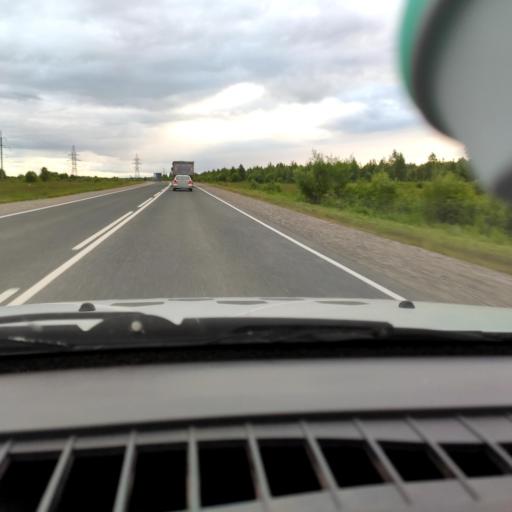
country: RU
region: Perm
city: Kalino
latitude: 58.2946
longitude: 57.4752
